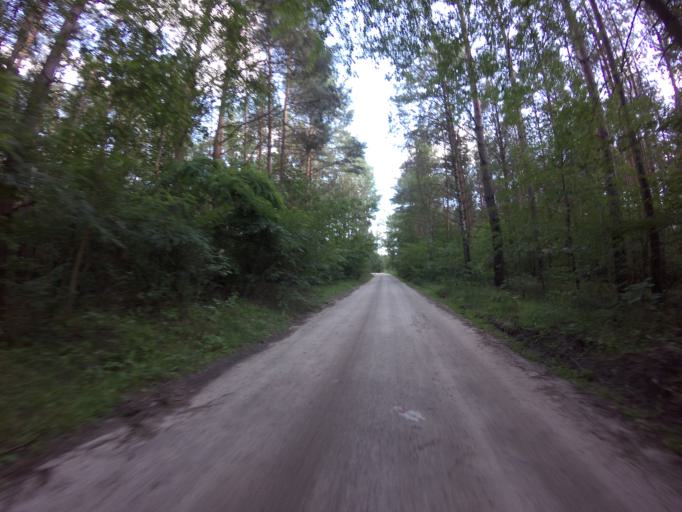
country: PL
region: Kujawsko-Pomorskie
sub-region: Powiat bydgoski
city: Koronowo
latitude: 53.3926
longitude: 17.9758
